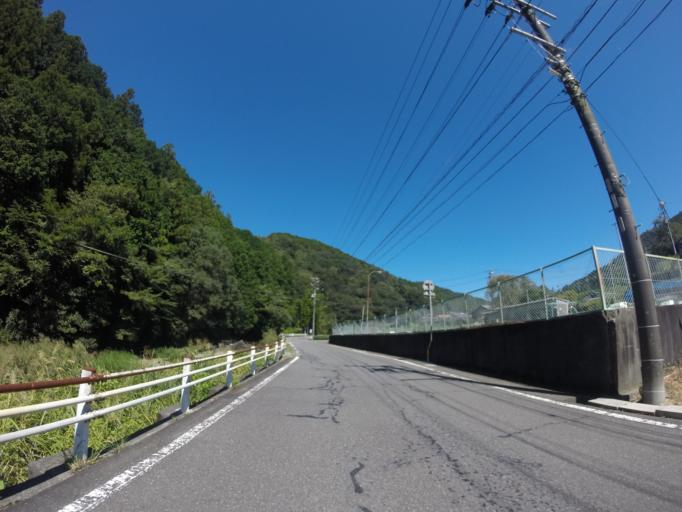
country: JP
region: Shizuoka
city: Kanaya
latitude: 34.9313
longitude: 138.1416
